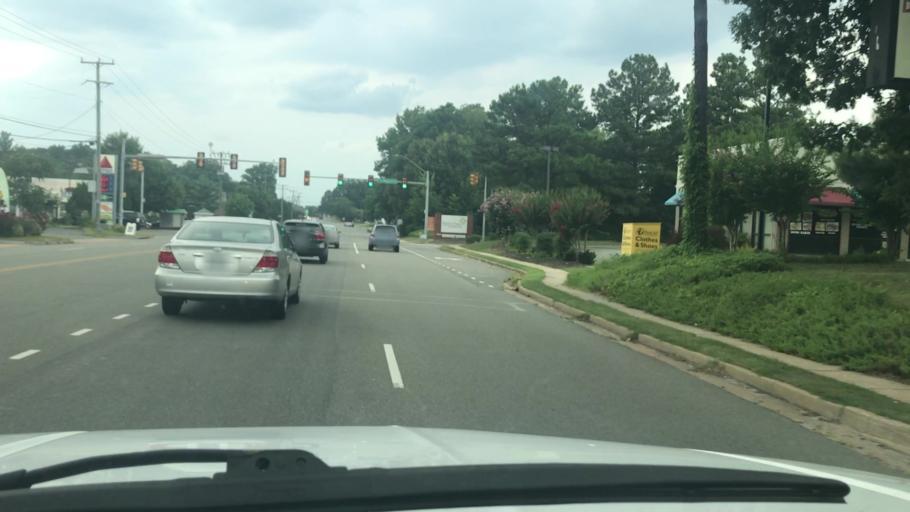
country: US
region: Virginia
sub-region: Henrico County
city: Tuckahoe
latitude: 37.6054
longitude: -77.5714
